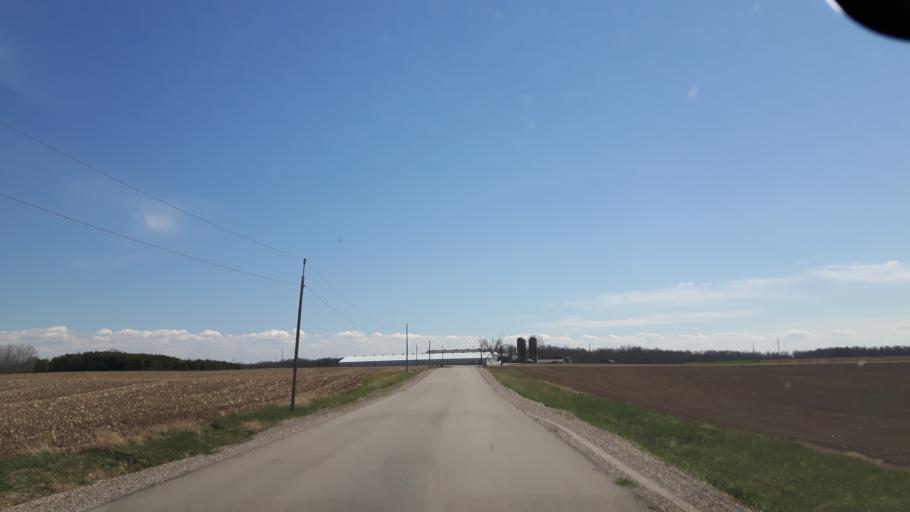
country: CA
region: Ontario
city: Bluewater
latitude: 43.5804
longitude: -81.6438
